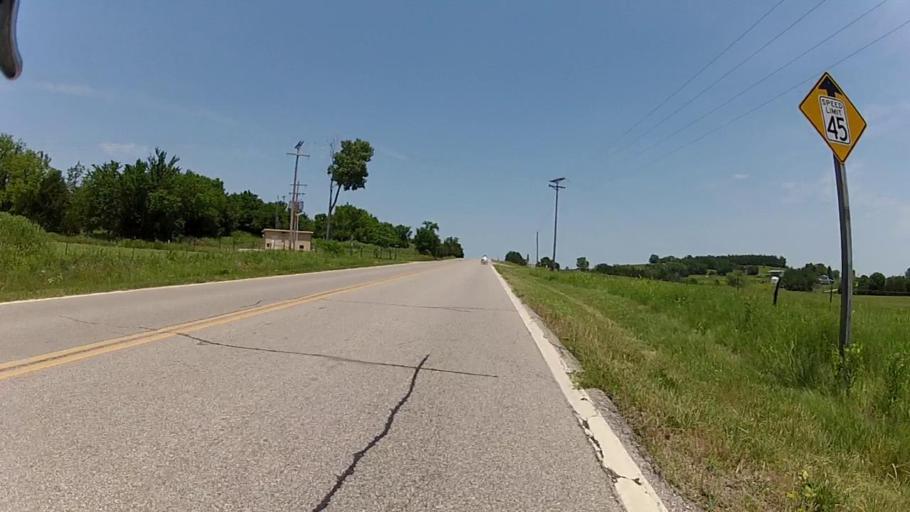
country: US
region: Kansas
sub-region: Chautauqua County
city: Sedan
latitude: 37.1224
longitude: -96.2067
